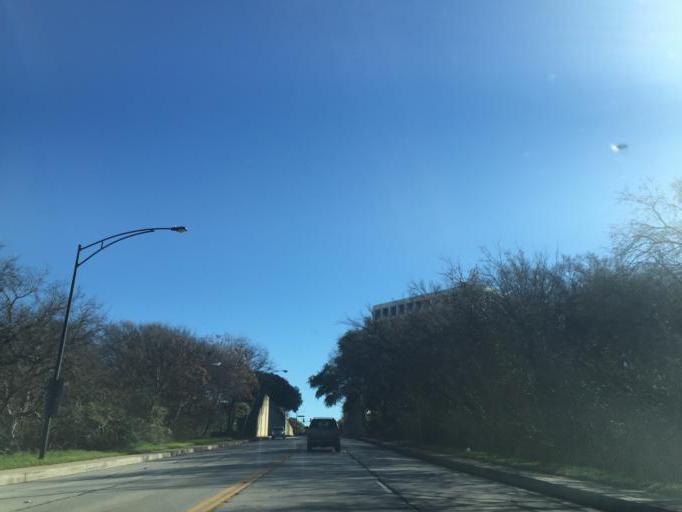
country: US
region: Texas
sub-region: Tarrant County
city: Fort Worth
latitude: 32.7467
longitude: -97.3442
